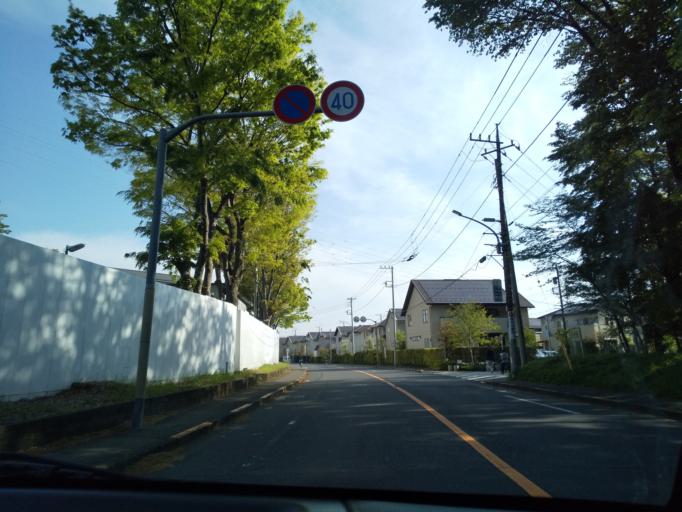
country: JP
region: Tokyo
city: Hino
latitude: 35.6661
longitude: 139.3852
